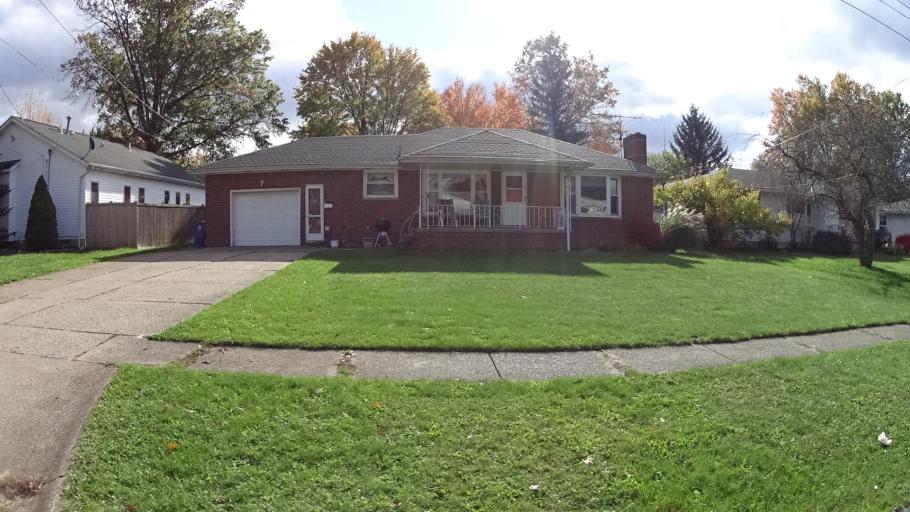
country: US
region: Ohio
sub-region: Lorain County
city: Lorain
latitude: 41.4369
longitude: -82.1800
